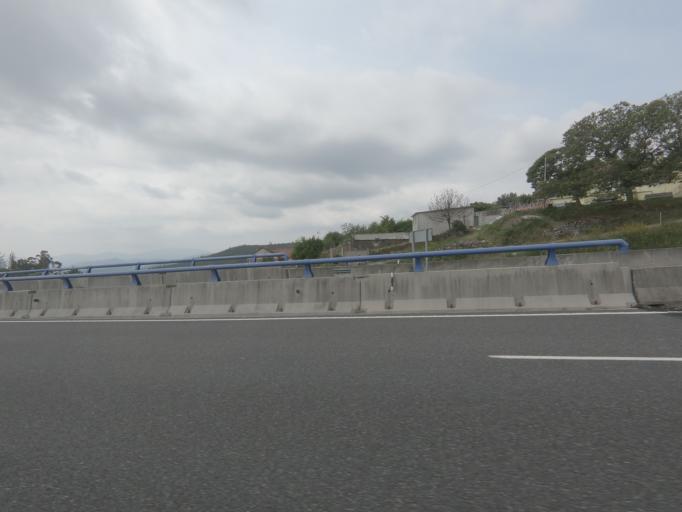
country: ES
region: Galicia
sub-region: Provincia de Pontevedra
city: Covelo
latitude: 42.1651
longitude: -8.3869
